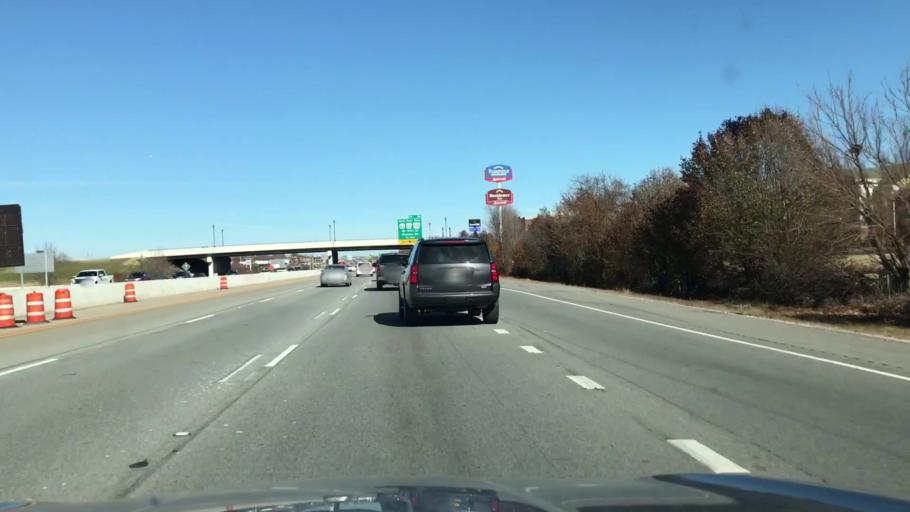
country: US
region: Arkansas
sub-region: Benton County
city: Bentonville
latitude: 36.3405
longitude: -94.1817
